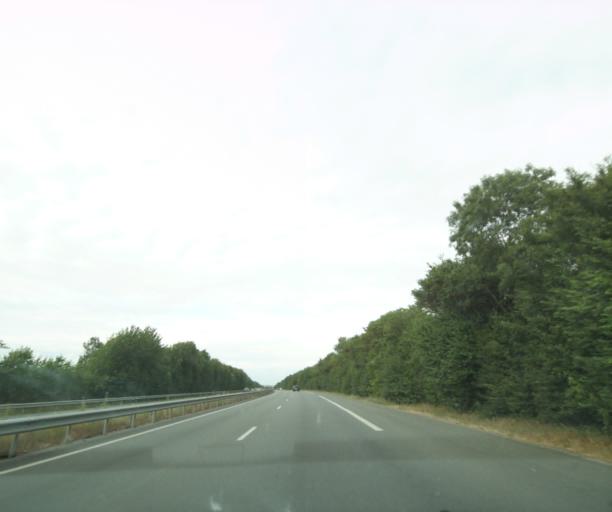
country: FR
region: Poitou-Charentes
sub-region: Departement de la Charente-Maritime
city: Dompierre-sur-Mer
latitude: 46.1849
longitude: -1.0785
